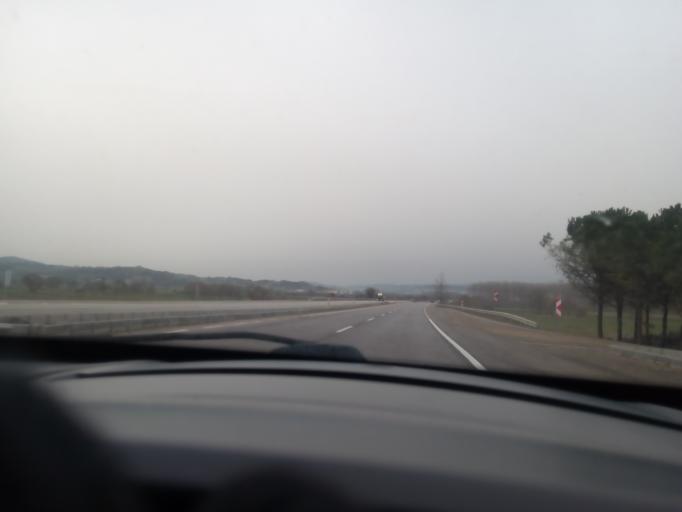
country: TR
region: Balikesir
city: Gobel
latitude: 39.9987
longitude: 28.2175
